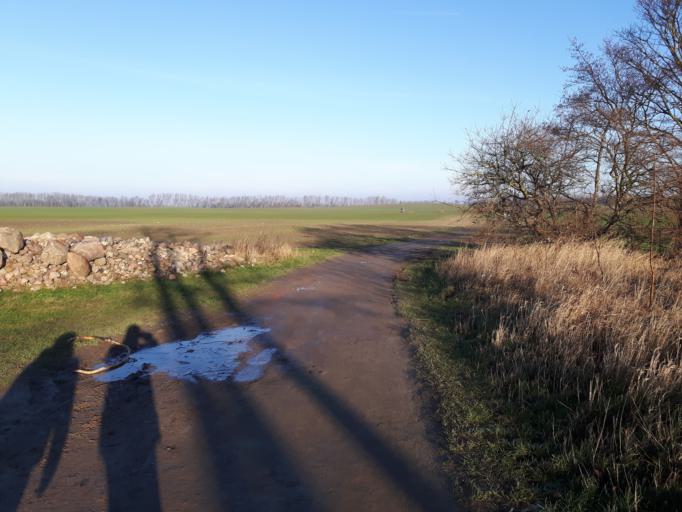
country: DE
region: Mecklenburg-Vorpommern
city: Altenkirchen
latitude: 54.6766
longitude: 13.4221
